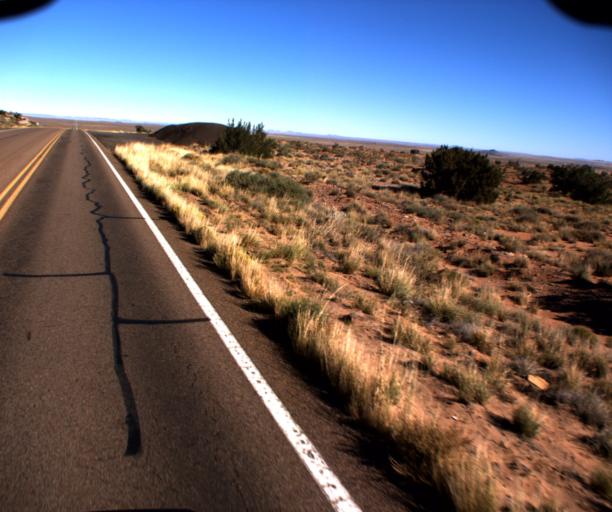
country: US
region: Arizona
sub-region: Navajo County
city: Snowflake
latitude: 34.6887
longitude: -110.1055
